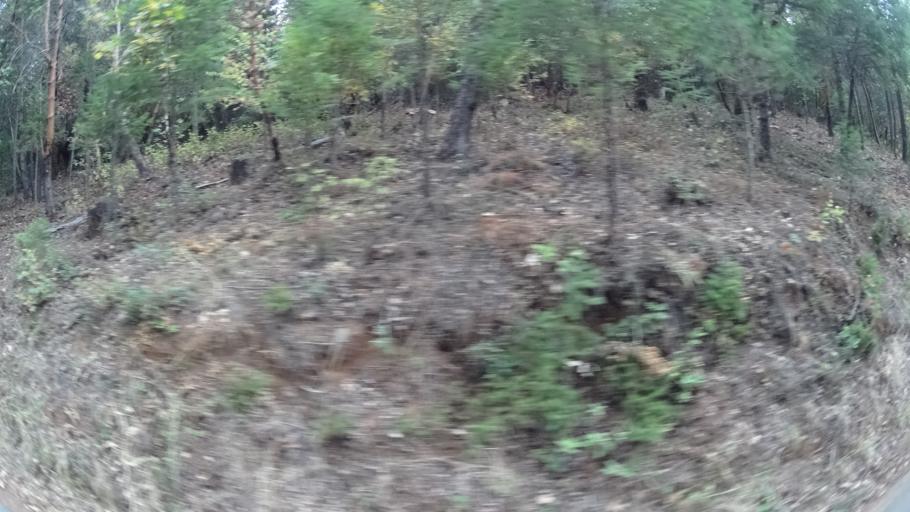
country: US
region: California
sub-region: Siskiyou County
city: Happy Camp
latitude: 41.7928
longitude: -123.3420
